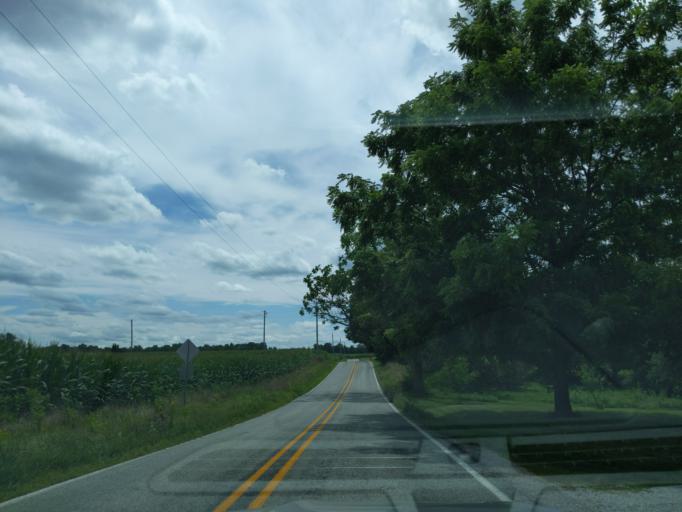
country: US
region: Indiana
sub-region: Ripley County
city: Osgood
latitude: 39.2106
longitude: -85.2753
